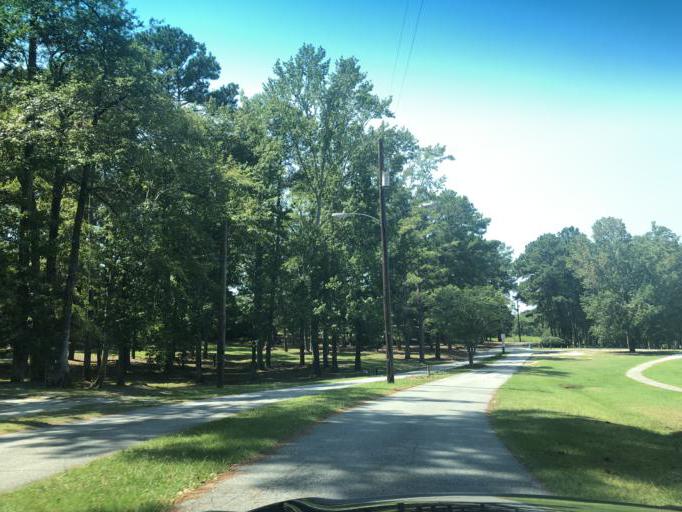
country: US
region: Georgia
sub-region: Muscogee County
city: Columbus
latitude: 32.5087
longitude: -84.9131
